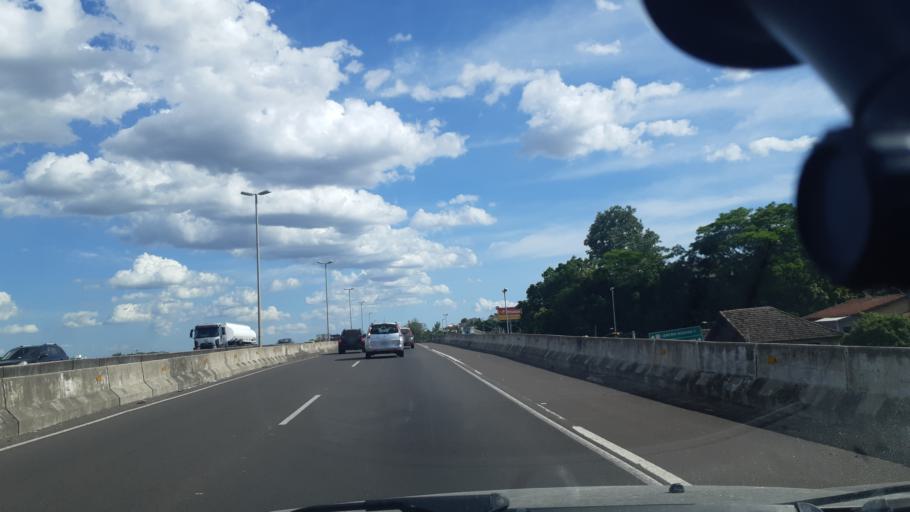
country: BR
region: Rio Grande do Sul
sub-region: Novo Hamburgo
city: Novo Hamburgo
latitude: -29.6690
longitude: -51.1432
